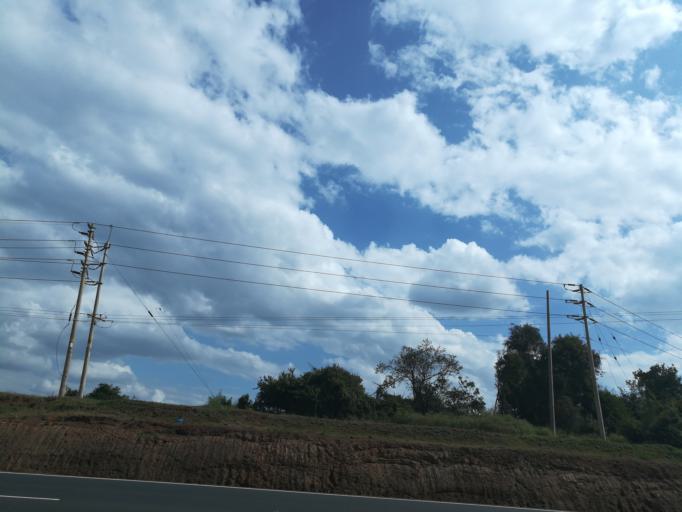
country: KE
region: Nairobi Area
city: Nairobi
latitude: -1.3230
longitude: 36.7380
